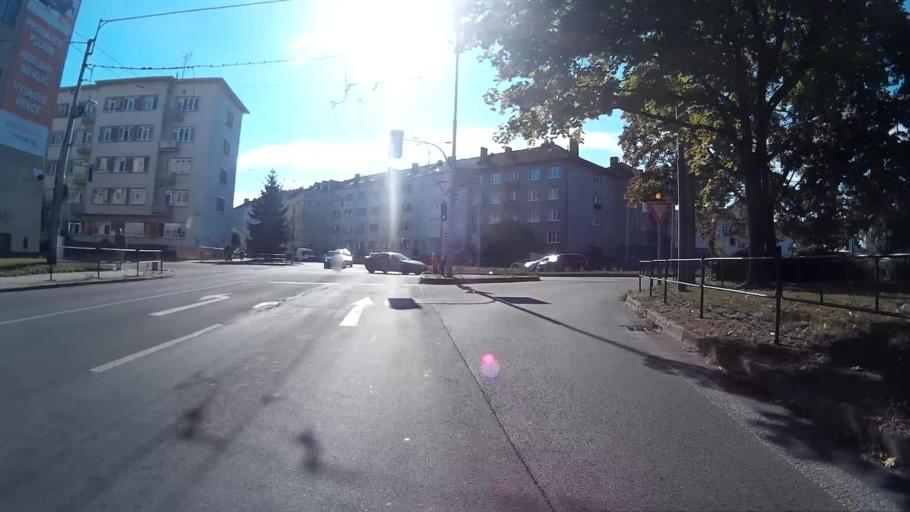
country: CZ
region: South Moravian
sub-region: Mesto Brno
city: Brno
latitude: 49.2127
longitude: 16.5896
